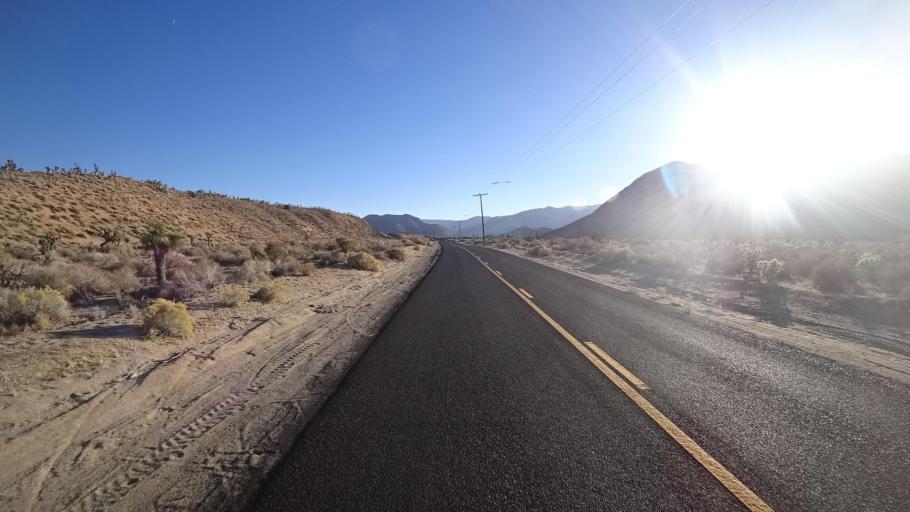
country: US
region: California
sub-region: Kern County
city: Weldon
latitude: 35.6194
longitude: -118.2435
